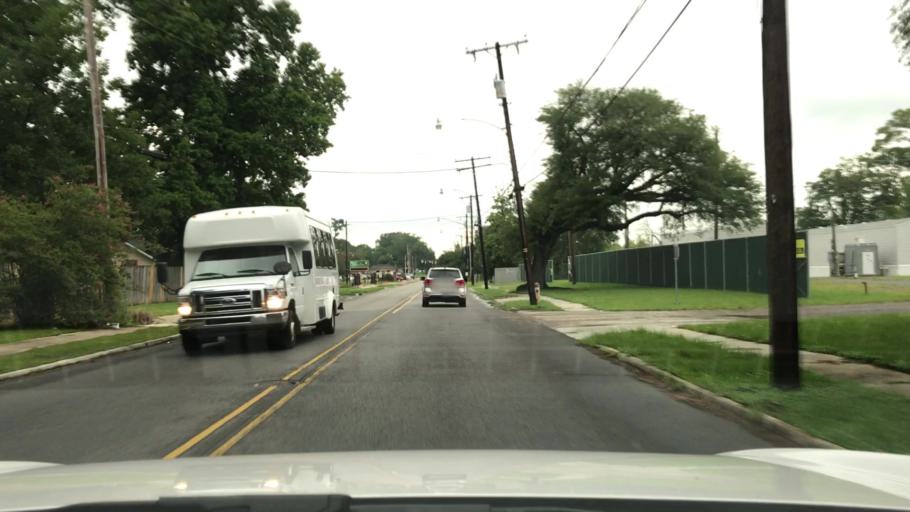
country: US
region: Louisiana
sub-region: East Baton Rouge Parish
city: Merrydale
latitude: 30.4770
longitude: -91.1174
